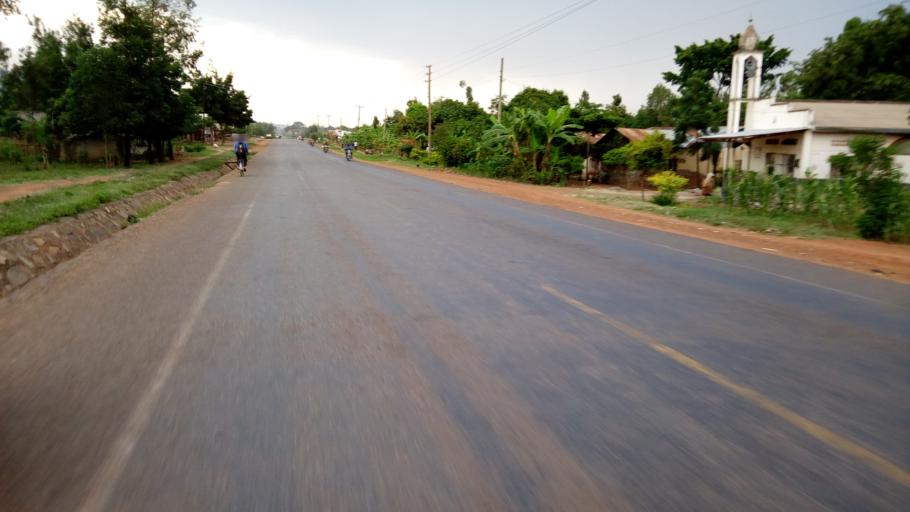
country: UG
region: Eastern Region
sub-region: Mbale District
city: Mbale
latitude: 1.1181
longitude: 34.1702
